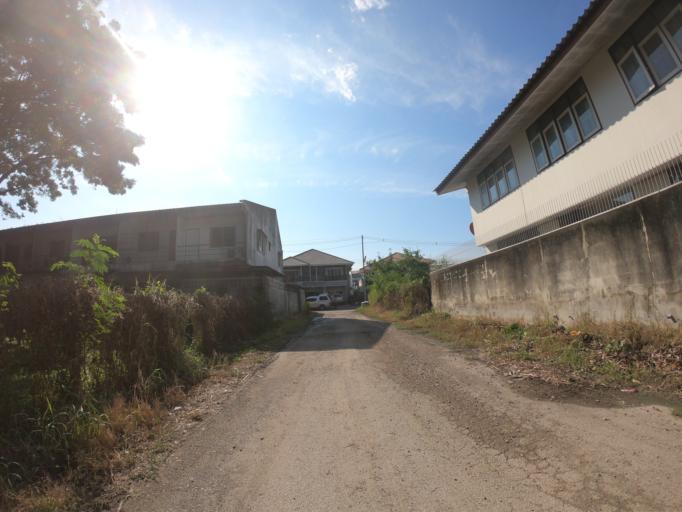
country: TH
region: Chiang Mai
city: Chiang Mai
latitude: 18.8097
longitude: 98.9911
